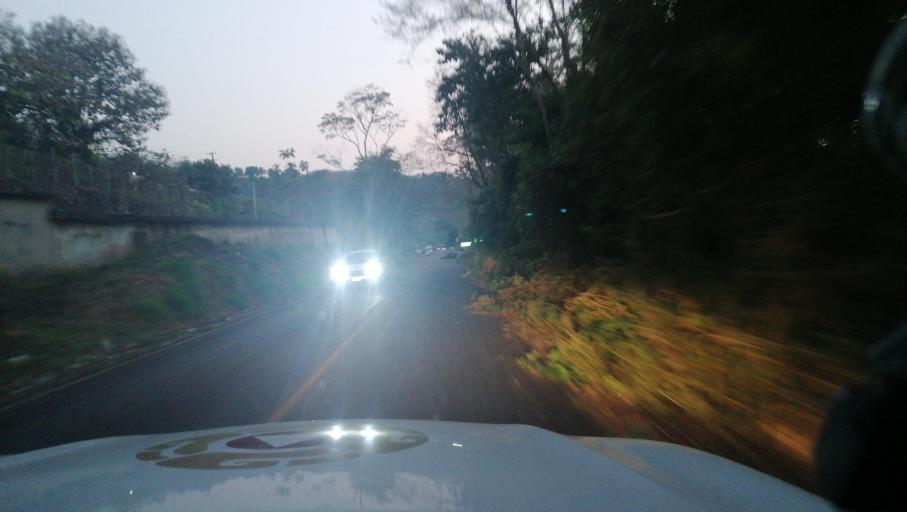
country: MX
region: Chiapas
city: Veinte de Noviembre
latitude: 14.9871
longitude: -92.2419
